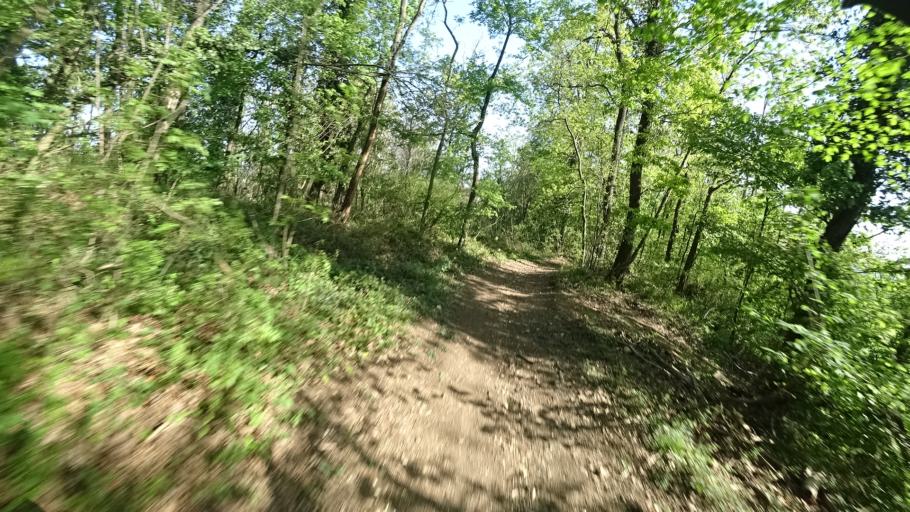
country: HR
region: Grad Zagreb
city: Stenjevec
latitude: 45.8481
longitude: 15.9152
